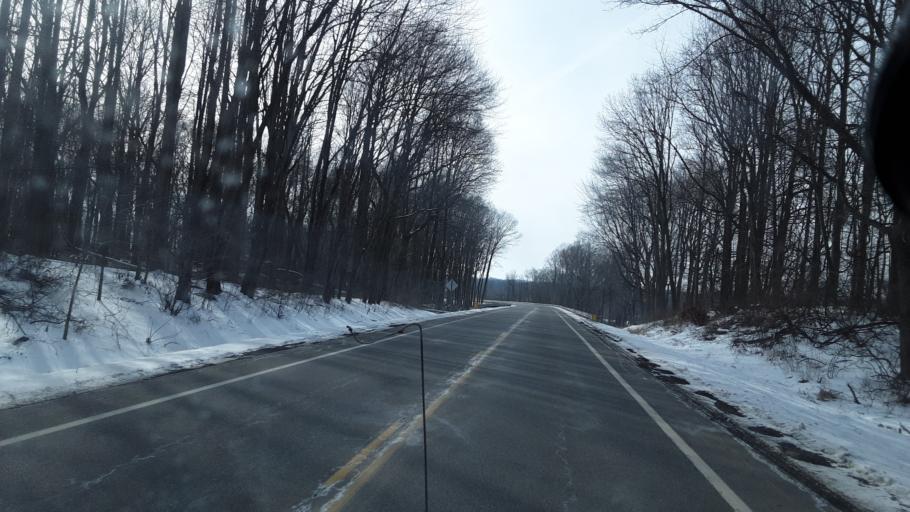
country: US
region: Ohio
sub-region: Stark County
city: Hartville
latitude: 41.0335
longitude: -81.2962
